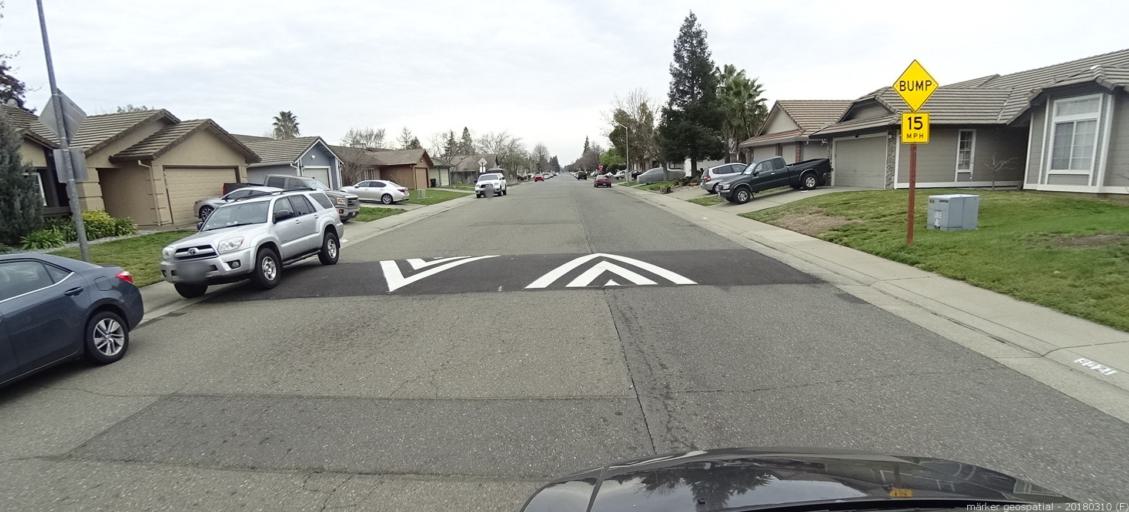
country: US
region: California
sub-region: Sacramento County
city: Vineyard
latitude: 38.4690
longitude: -121.3663
